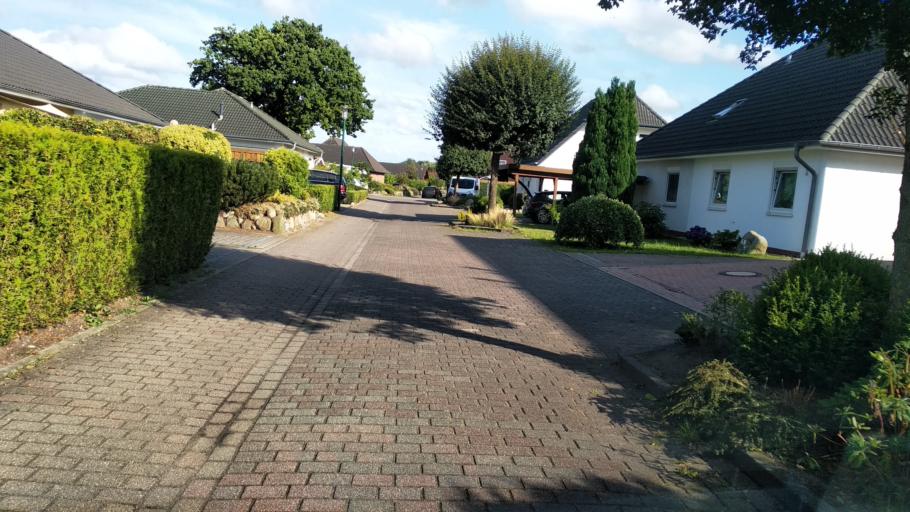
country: DE
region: Schleswig-Holstein
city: Busdorf
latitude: 54.4859
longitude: 9.5426
